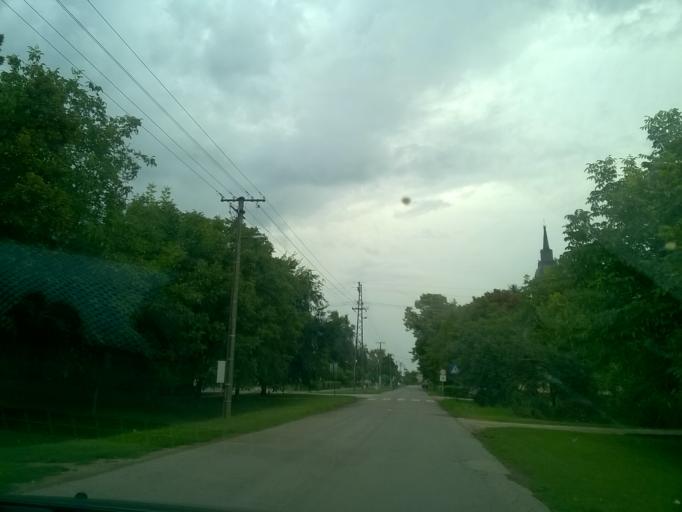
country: RS
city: Tomasevac
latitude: 45.2665
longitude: 20.6198
